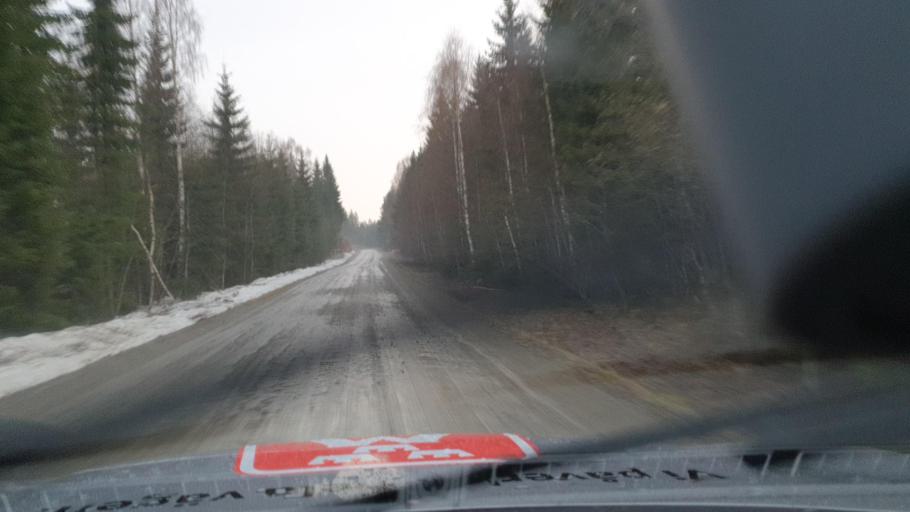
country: SE
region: Vaesternorrland
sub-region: OErnskoeldsviks Kommun
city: Bjasta
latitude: 63.2118
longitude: 18.3468
